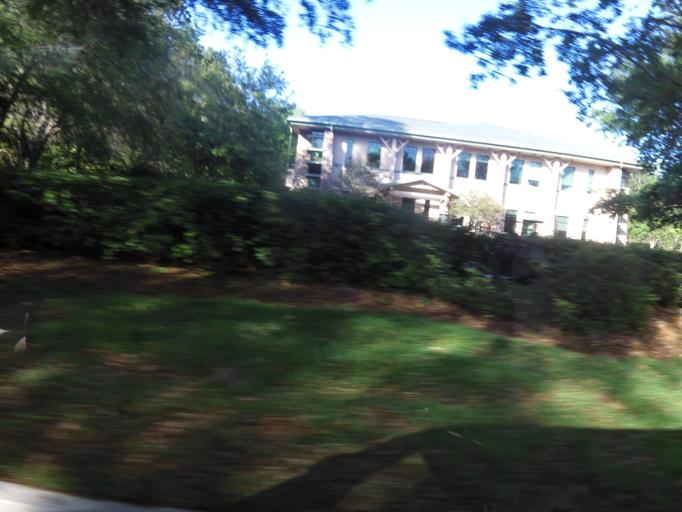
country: US
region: Florida
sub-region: Saint Johns County
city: Villano Beach
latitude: 29.9856
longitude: -81.4687
